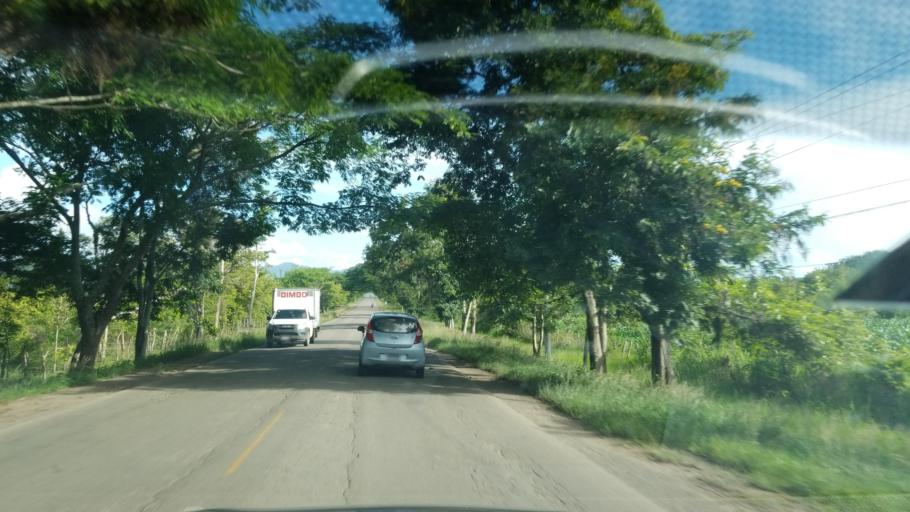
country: HN
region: El Paraiso
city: Arauli
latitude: 13.9253
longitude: -86.5579
